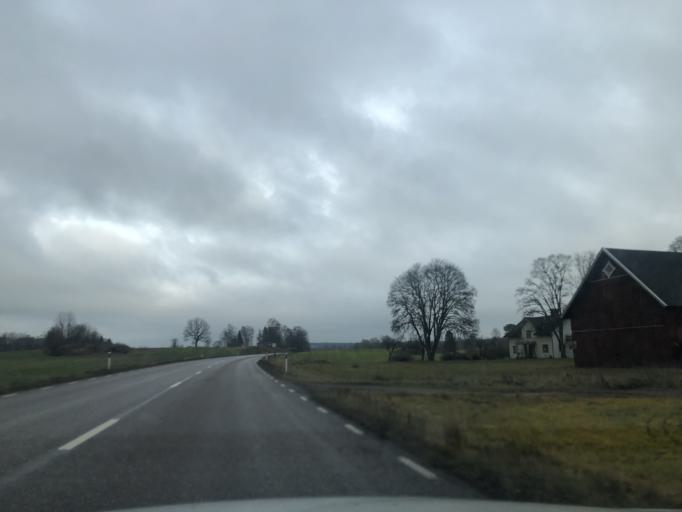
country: SE
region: Vaestra Goetaland
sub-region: Ulricehamns Kommun
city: Ulricehamn
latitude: 57.8917
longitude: 13.4423
